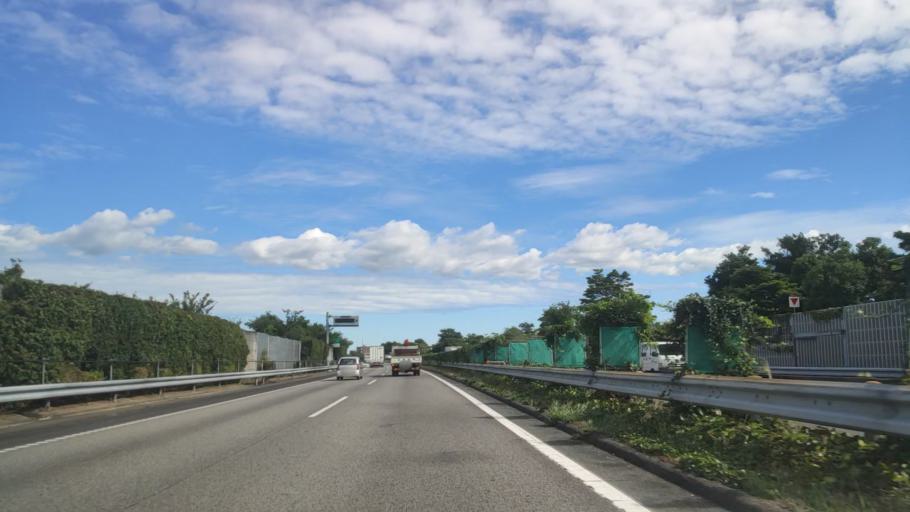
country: JP
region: Shizuoka
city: Hamamatsu
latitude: 34.7517
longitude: 137.7470
